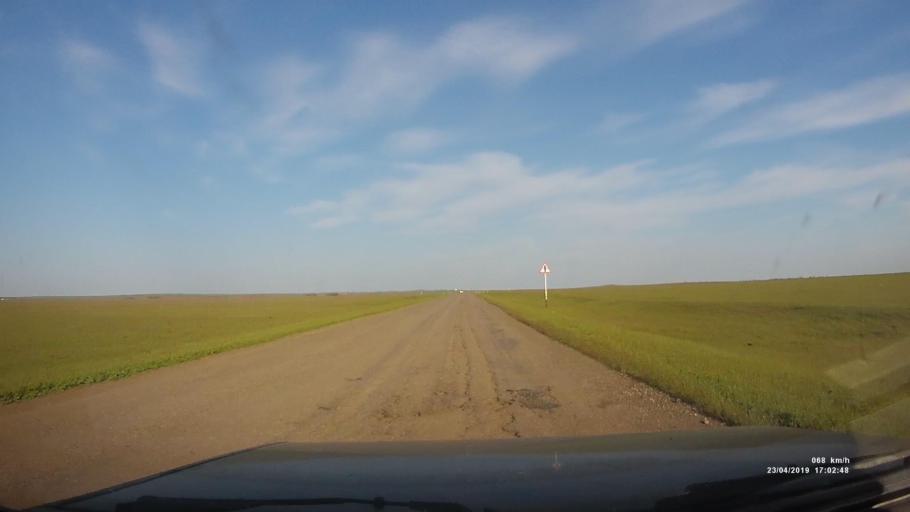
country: RU
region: Kalmykiya
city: Priyutnoye
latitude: 46.2915
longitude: 43.4228
